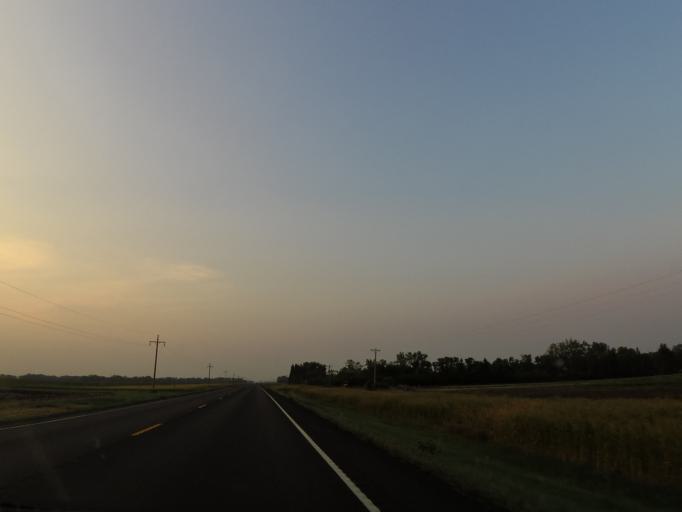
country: US
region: North Dakota
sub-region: Walsh County
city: Park River
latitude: 48.2804
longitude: -97.6224
